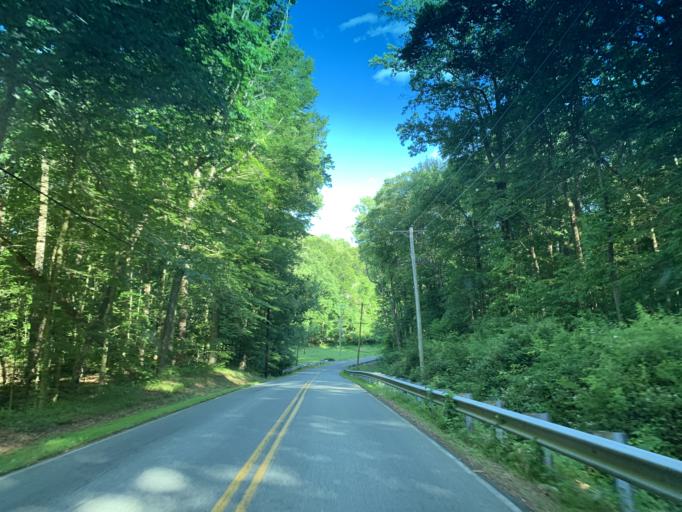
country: US
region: Maryland
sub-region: Cecil County
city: Perryville
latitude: 39.5920
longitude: -76.0833
